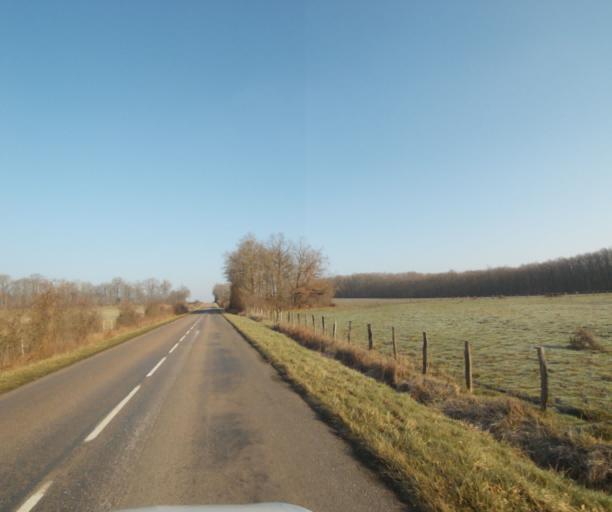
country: FR
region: Champagne-Ardenne
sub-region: Departement de la Haute-Marne
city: Montier-en-Der
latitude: 48.4285
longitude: 4.7504
